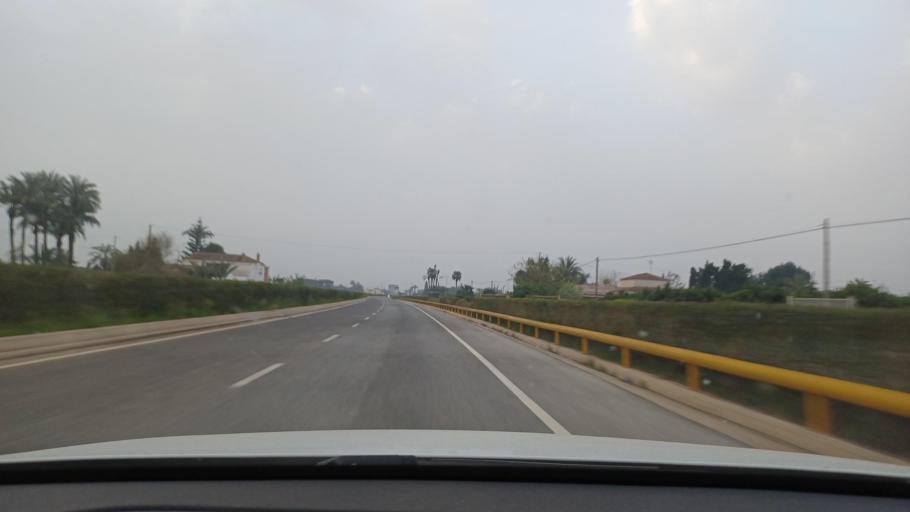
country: ES
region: Valencia
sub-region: Provincia de Alicante
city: Elche
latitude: 38.1933
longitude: -0.7011
